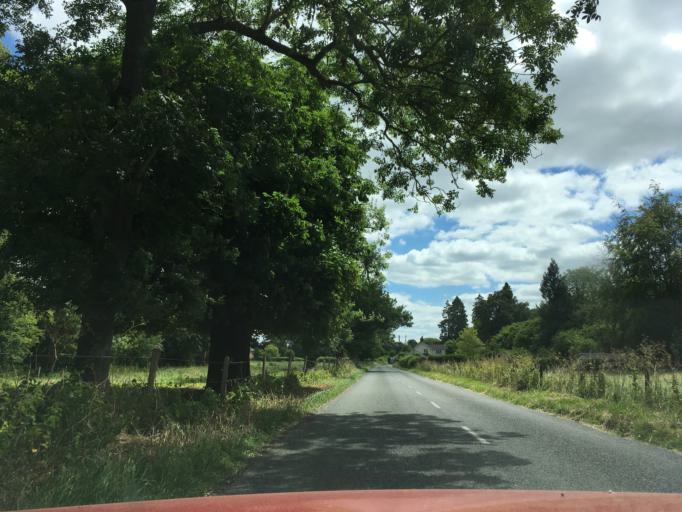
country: GB
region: England
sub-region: Hampshire
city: Andover
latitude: 51.2625
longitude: -1.4214
